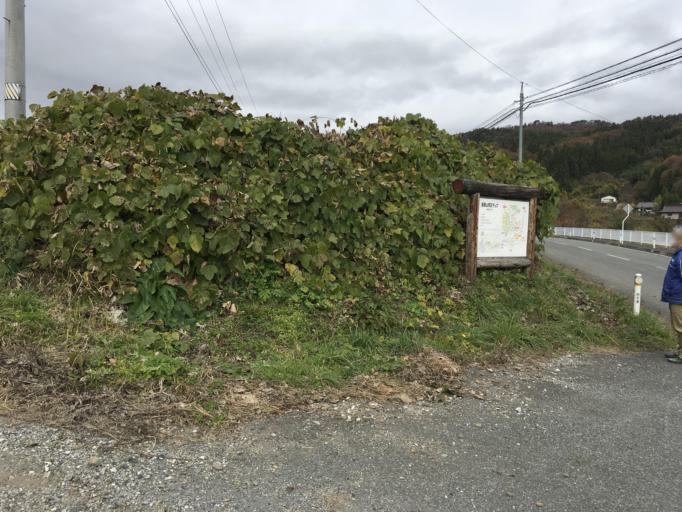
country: JP
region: Iwate
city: Mizusawa
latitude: 39.0816
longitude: 141.3534
